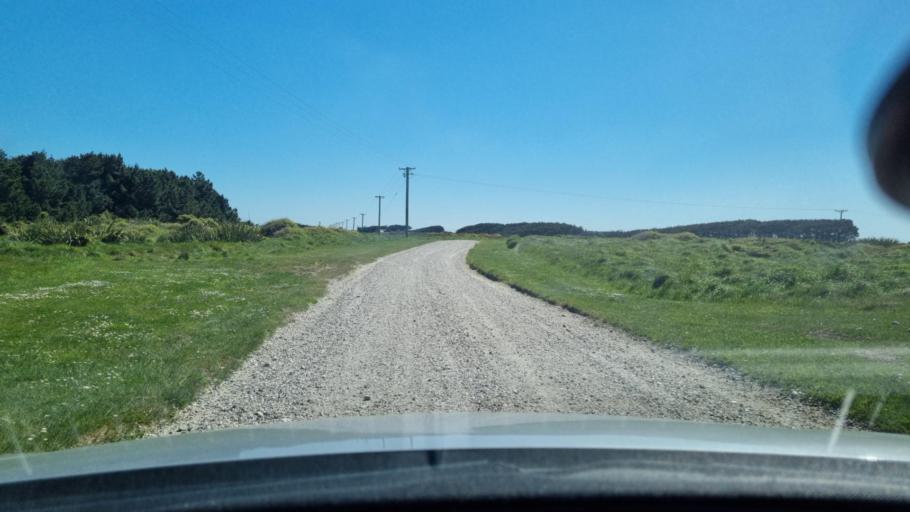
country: NZ
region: Southland
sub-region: Invercargill City
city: Invercargill
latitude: -46.4359
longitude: 168.2378
